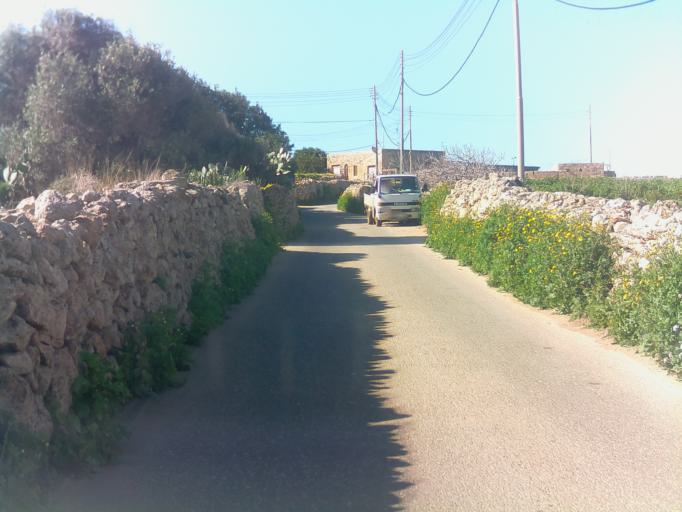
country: MT
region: L-Imgarr
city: Imgarr
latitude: 35.9138
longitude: 14.3566
